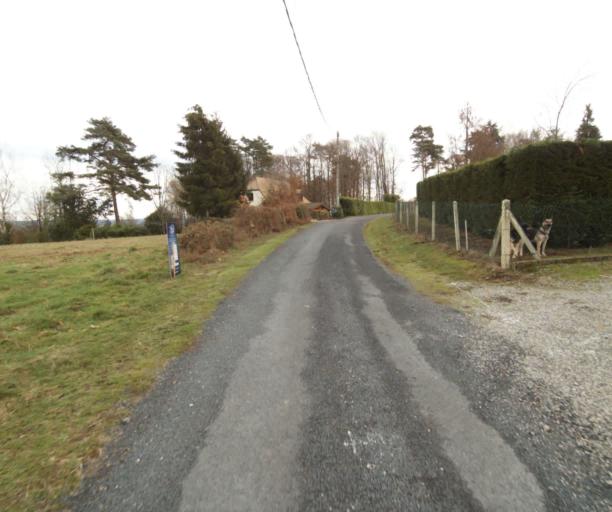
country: FR
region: Limousin
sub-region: Departement de la Correze
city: Chameyrat
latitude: 45.2661
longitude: 1.6970
